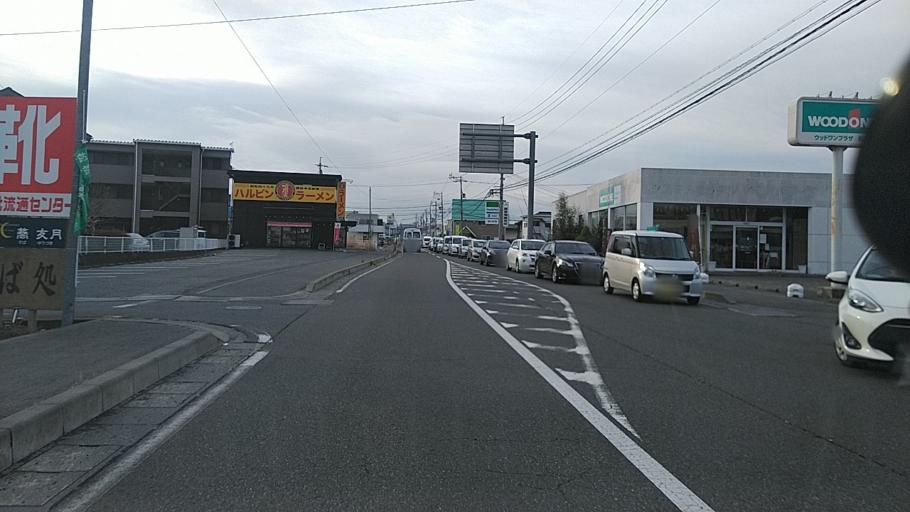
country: JP
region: Nagano
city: Matsumoto
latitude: 36.2134
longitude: 137.9796
